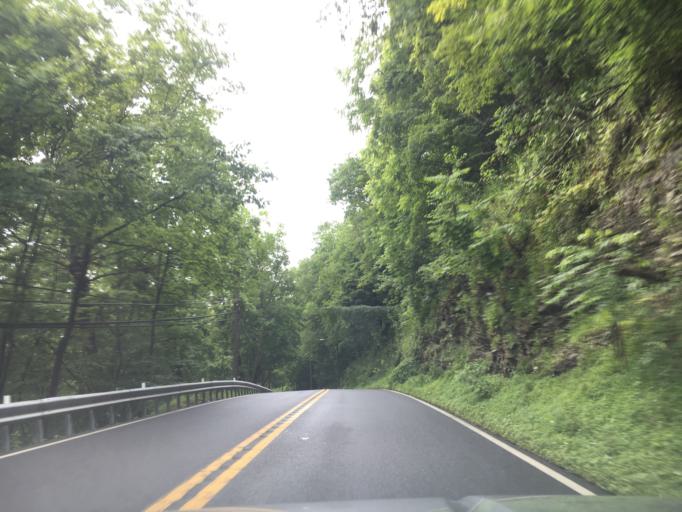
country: US
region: Pennsylvania
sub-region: Lehigh County
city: Cementon
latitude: 40.6967
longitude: -75.5134
